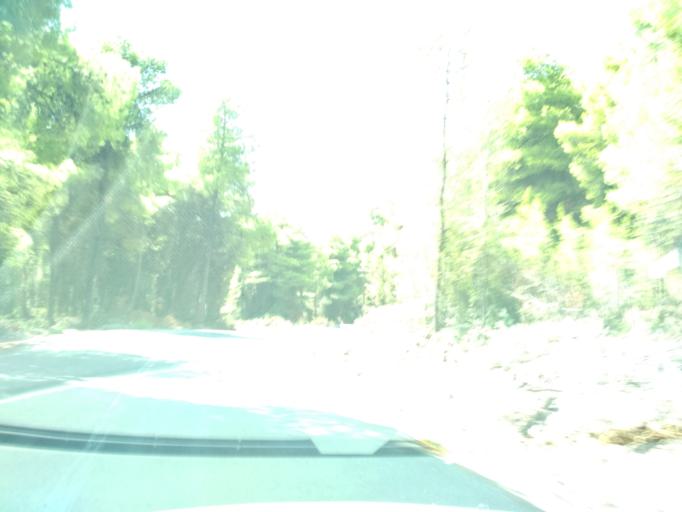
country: GR
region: Central Greece
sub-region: Nomos Evvoias
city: Roviai
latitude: 38.8225
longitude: 23.2410
